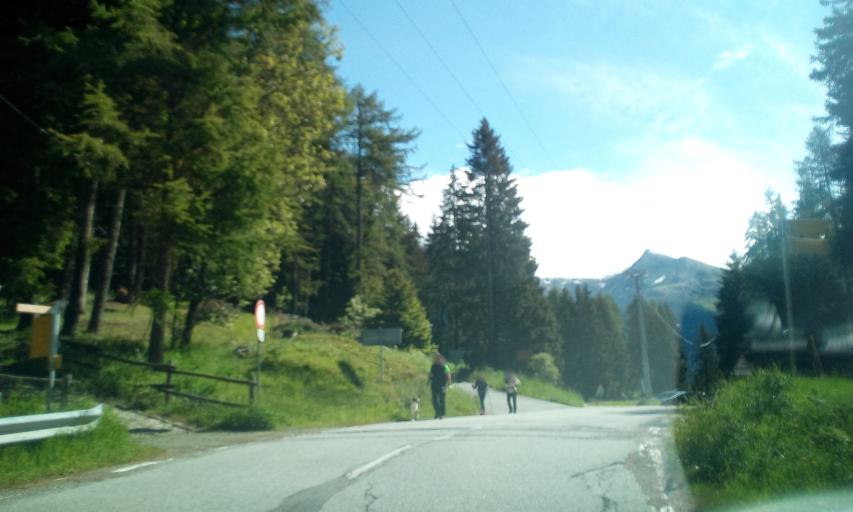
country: IT
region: Aosta Valley
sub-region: Valle d'Aosta
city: Brusson
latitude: 45.7538
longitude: 7.7029
